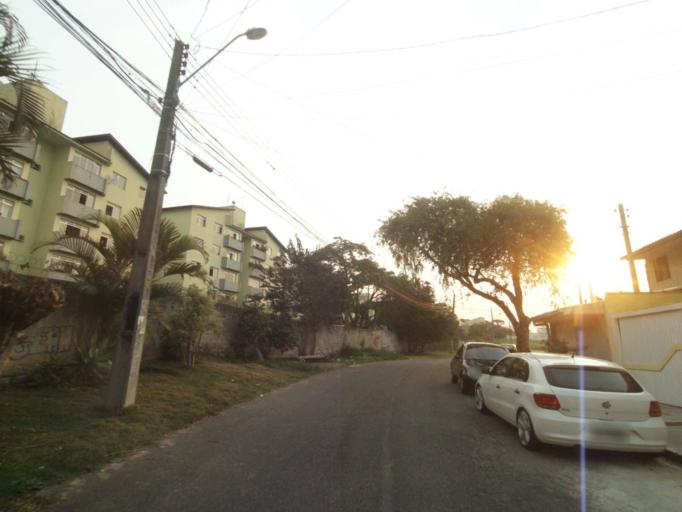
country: BR
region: Parana
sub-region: Curitiba
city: Curitiba
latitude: -25.4750
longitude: -49.2804
